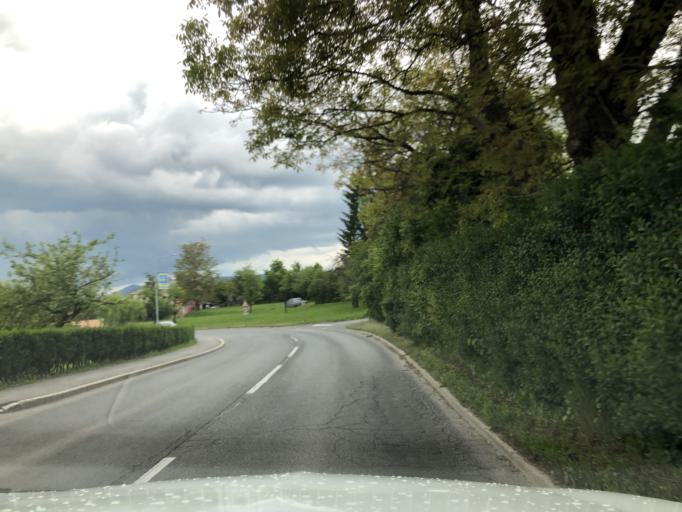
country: SI
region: Cerknica
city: Rakek
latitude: 45.8102
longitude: 14.3257
